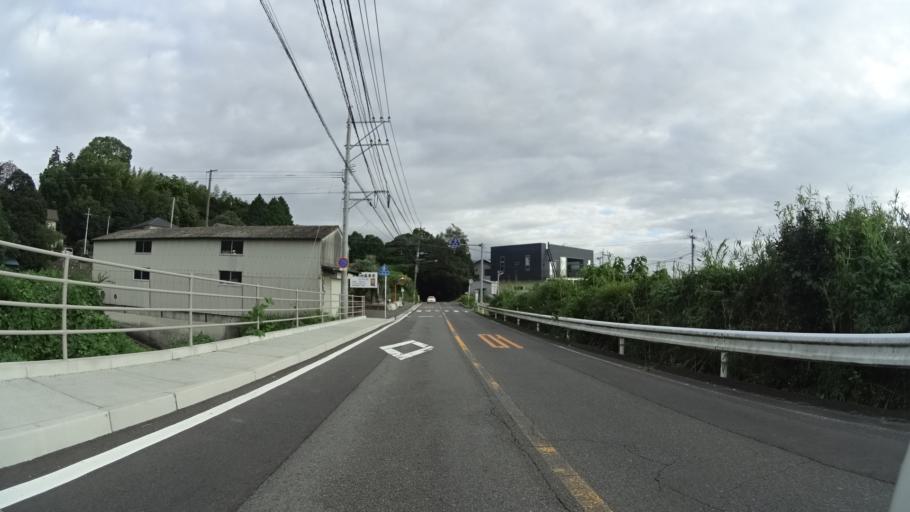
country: JP
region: Oita
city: Beppu
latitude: 33.3232
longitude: 131.4785
